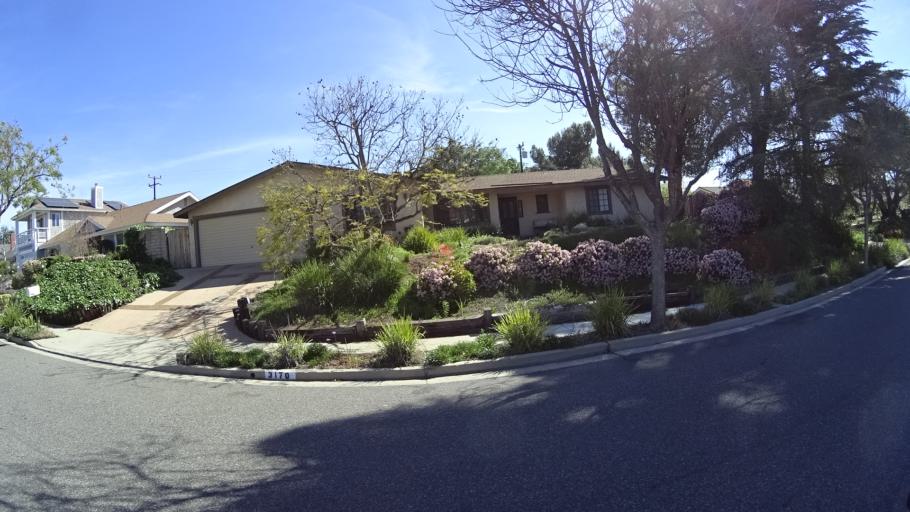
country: US
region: California
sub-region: Ventura County
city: Thousand Oaks
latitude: 34.2236
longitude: -118.8628
